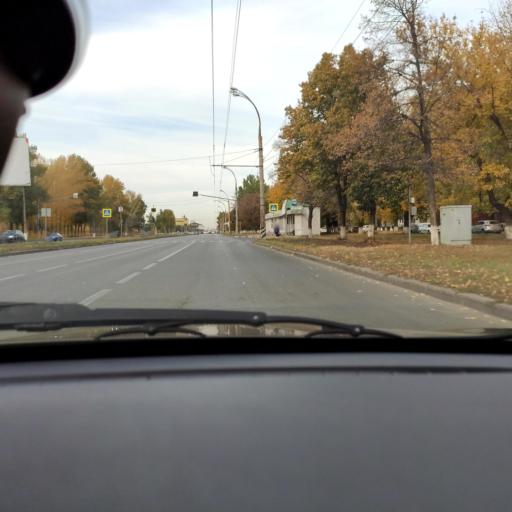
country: RU
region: Samara
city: Tol'yatti
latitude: 53.5140
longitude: 49.2577
